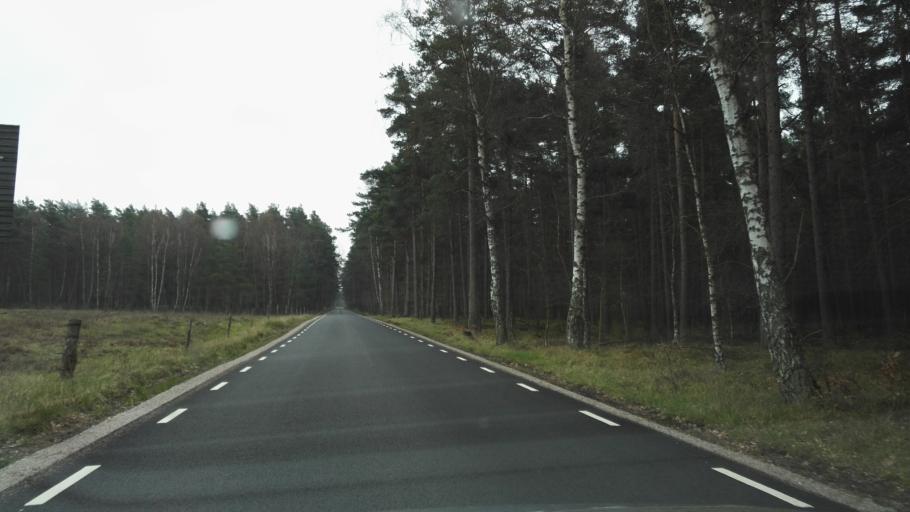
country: SE
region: Skane
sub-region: Simrishamns Kommun
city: Simrishamn
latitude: 55.3939
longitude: 14.1800
